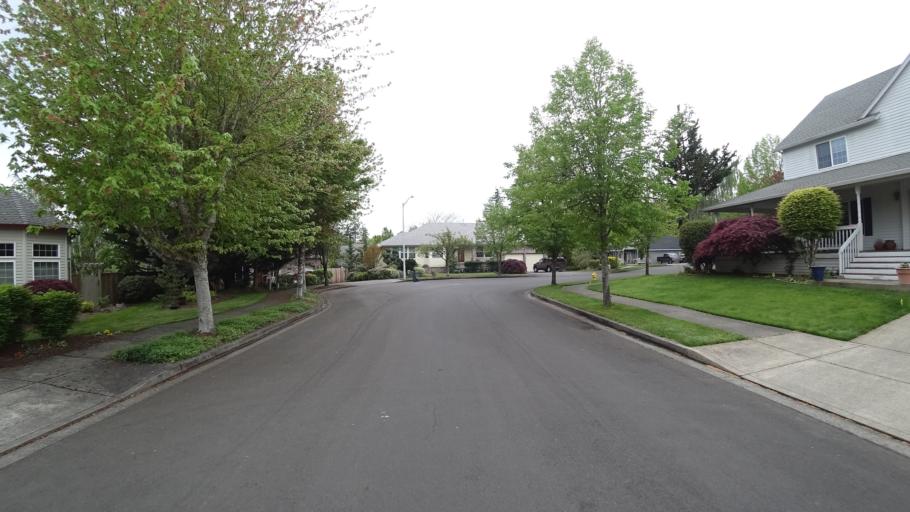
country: US
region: Oregon
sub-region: Washington County
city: Hillsboro
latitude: 45.5474
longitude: -122.9714
